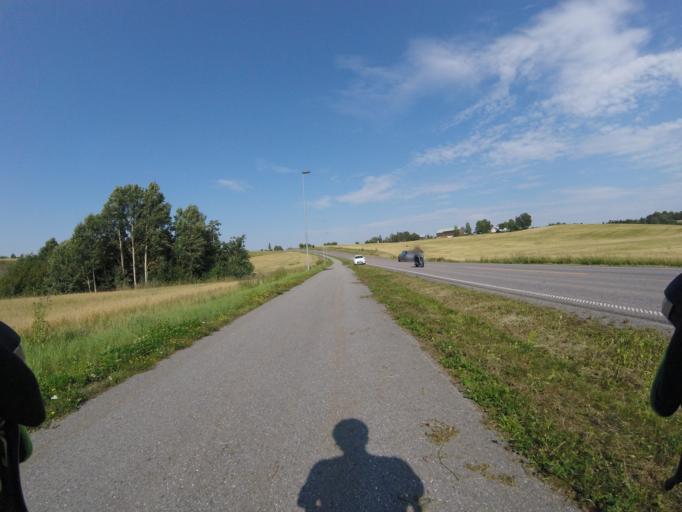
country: NO
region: Akershus
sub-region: Sorum
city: Frogner
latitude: 60.0121
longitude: 11.1110
